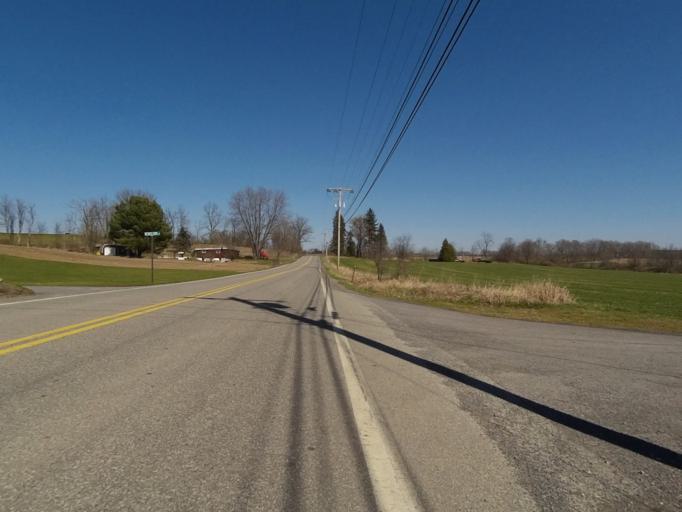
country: US
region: Pennsylvania
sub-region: Centre County
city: Stormstown
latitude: 40.7827
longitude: -78.0332
